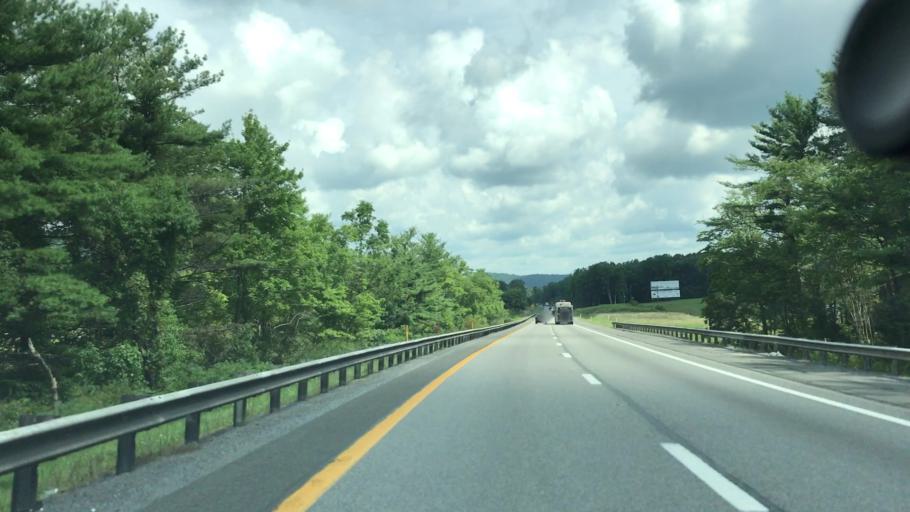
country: US
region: West Virginia
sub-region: Mercer County
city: Athens
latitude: 37.4464
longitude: -81.0663
